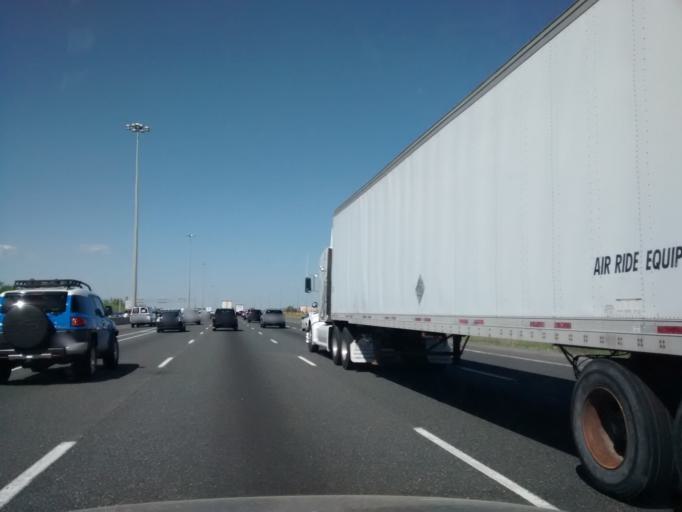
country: CA
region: Ontario
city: Burlington
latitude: 43.3961
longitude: -79.7554
